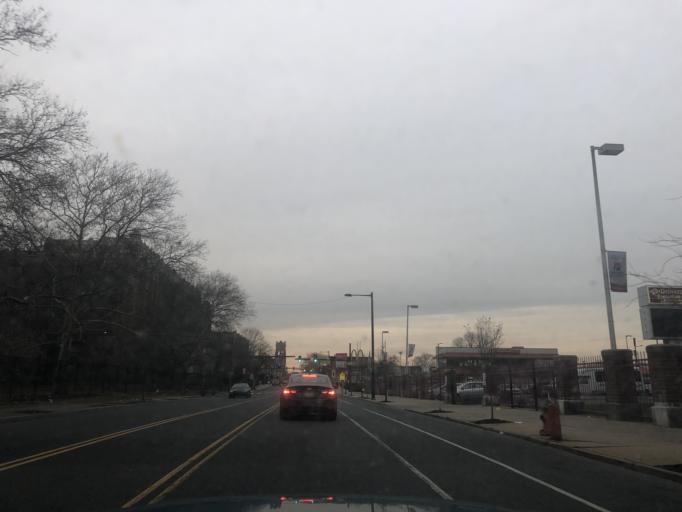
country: US
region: Pennsylvania
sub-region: Philadelphia County
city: Philadelphia
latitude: 39.9953
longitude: -75.1647
